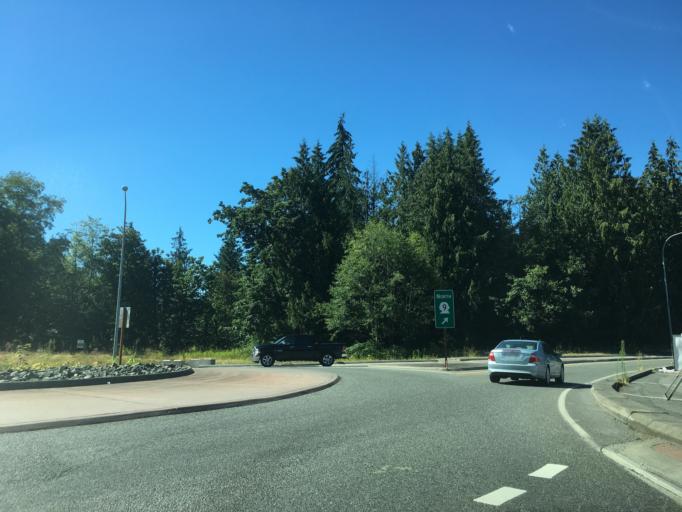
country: US
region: Washington
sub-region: Skagit County
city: Big Lake
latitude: 48.4300
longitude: -122.2643
